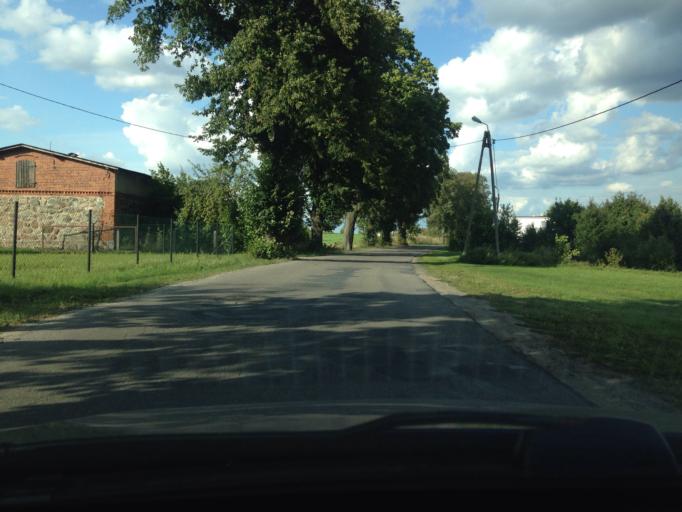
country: PL
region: Kujawsko-Pomorskie
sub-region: Powiat brodnicki
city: Gorzno
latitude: 53.1904
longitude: 19.6408
